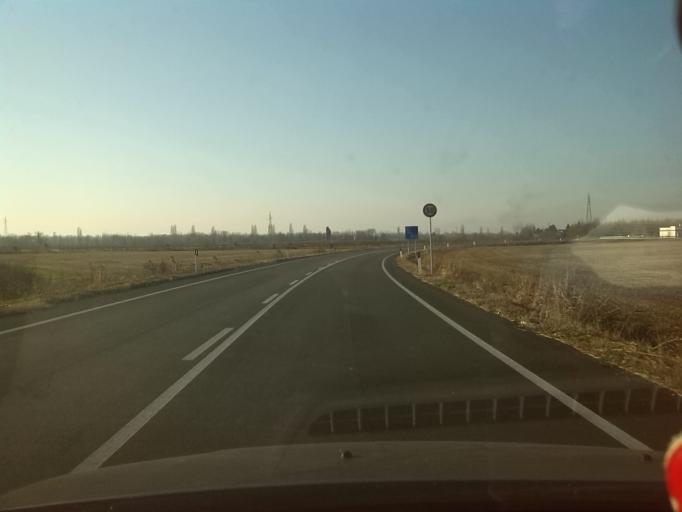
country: IT
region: Friuli Venezia Giulia
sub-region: Provincia di Udine
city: Manzano
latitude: 45.9777
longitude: 13.3570
